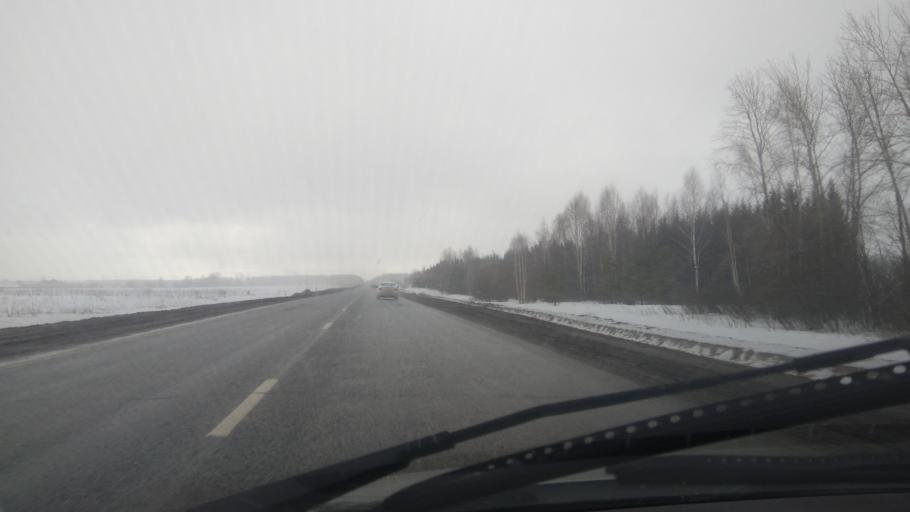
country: RU
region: Perm
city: Orda
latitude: 57.2985
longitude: 56.9863
